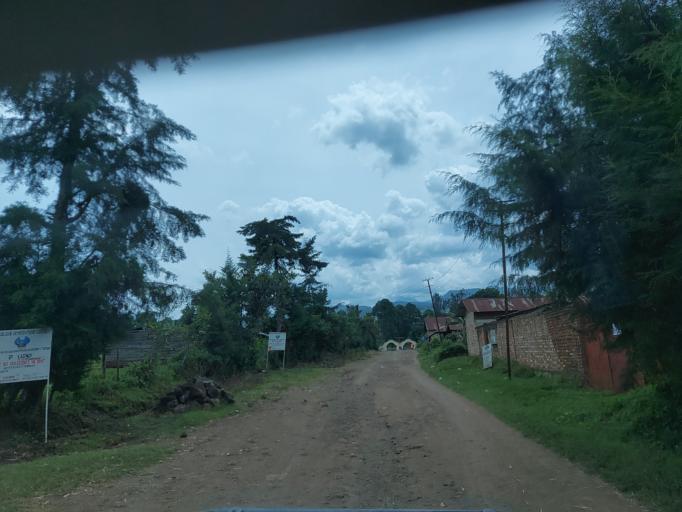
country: CD
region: South Kivu
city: Bukavu
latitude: -2.2440
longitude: 28.8155
